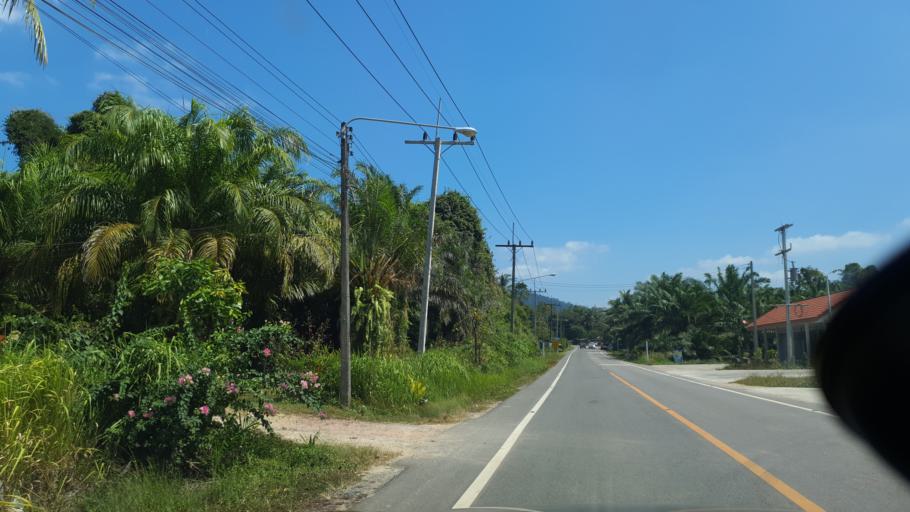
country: TH
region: Krabi
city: Khlong Thom
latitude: 7.9204
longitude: 99.2531
